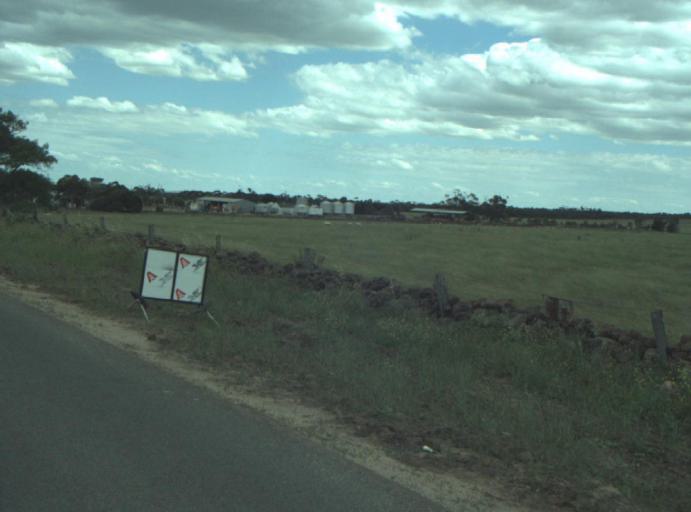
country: AU
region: Victoria
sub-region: Wyndham
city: Little River
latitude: -37.9475
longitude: 144.4656
